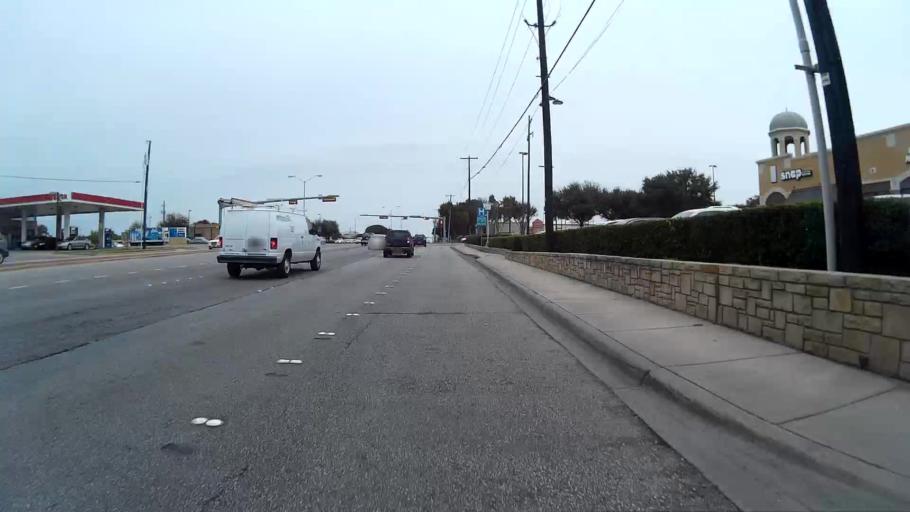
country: US
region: Texas
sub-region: Dallas County
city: Richardson
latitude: 32.9775
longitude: -96.7680
